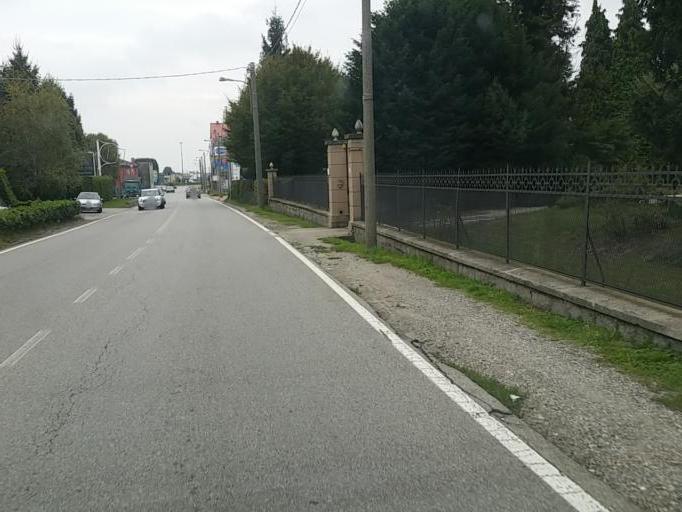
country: IT
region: Piedmont
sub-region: Provincia di Novara
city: Gozzano
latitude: 45.7389
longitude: 8.4389
